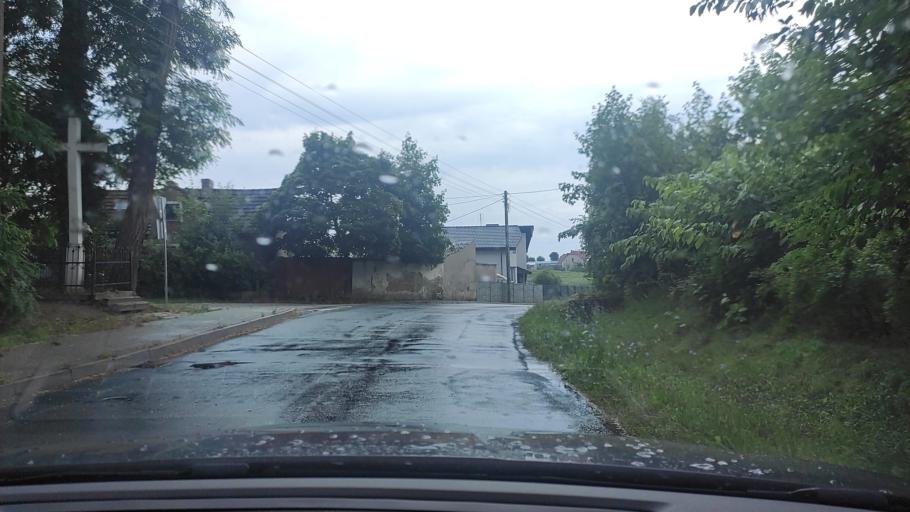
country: PL
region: Greater Poland Voivodeship
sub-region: Powiat poznanski
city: Kleszczewo
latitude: 52.2986
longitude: 17.1251
